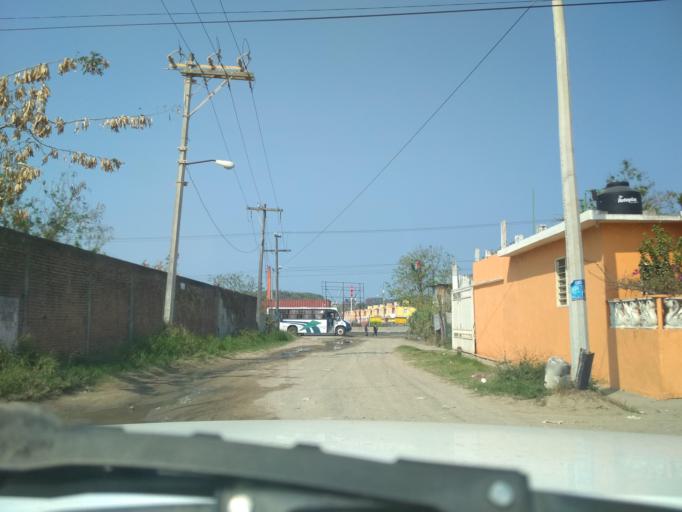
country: MX
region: Veracruz
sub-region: Veracruz
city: Colonia Chalchihuecan
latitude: 19.2149
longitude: -96.2129
